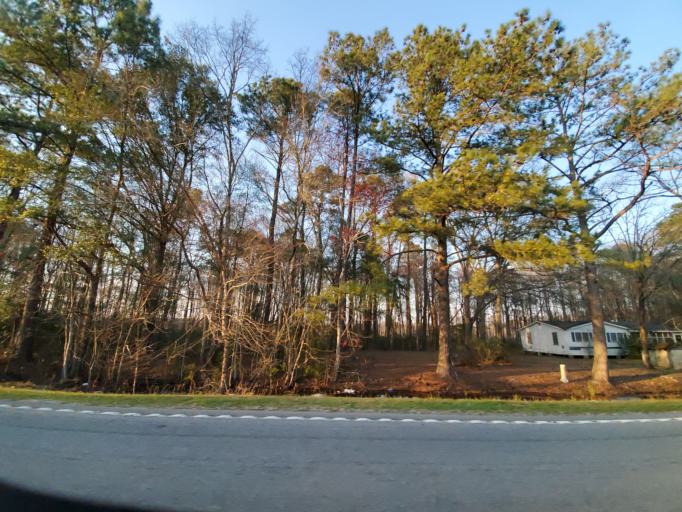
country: US
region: South Carolina
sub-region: Dorchester County
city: Ridgeville
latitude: 33.0517
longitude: -80.4756
